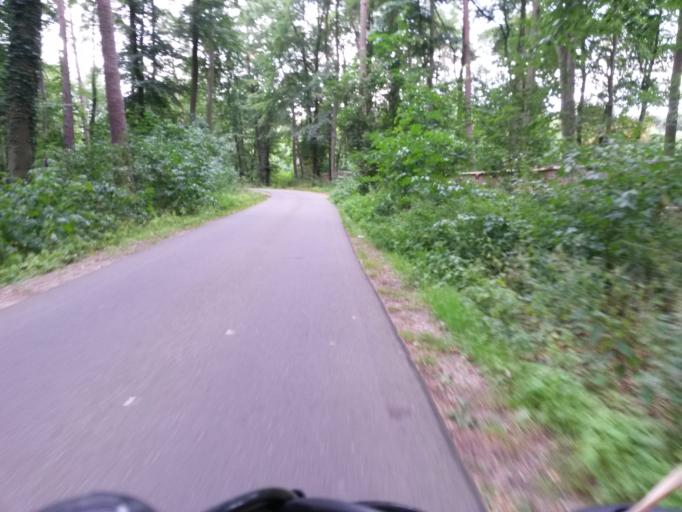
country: DE
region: Brandenburg
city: Angermunde
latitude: 53.0545
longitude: 13.9397
